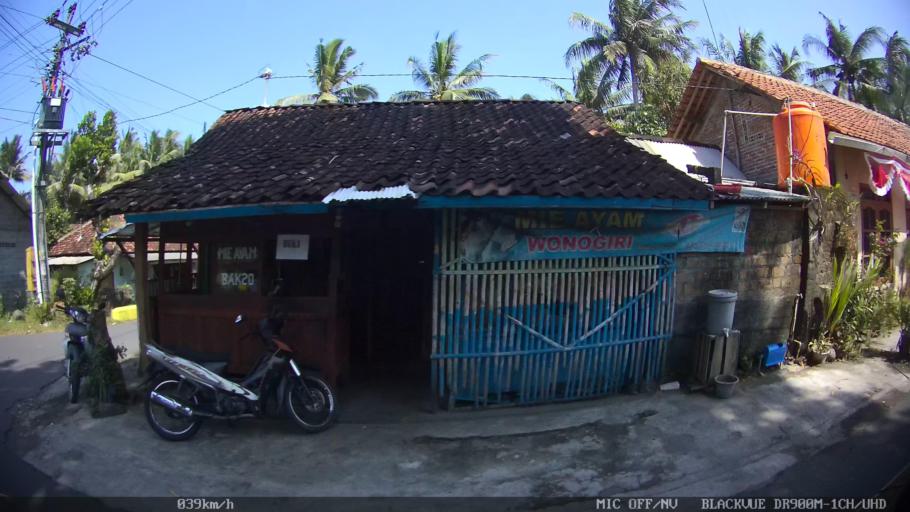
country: ID
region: Daerah Istimewa Yogyakarta
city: Srandakan
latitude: -7.9082
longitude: 110.1523
